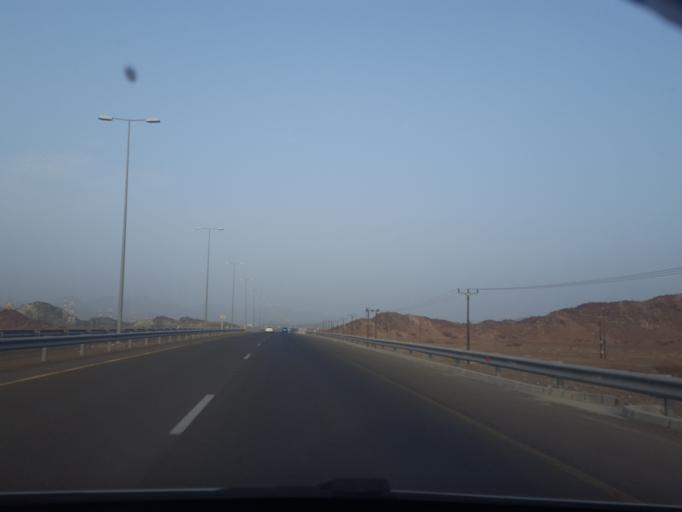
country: OM
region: Al Buraimi
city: Al Buraymi
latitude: 24.2467
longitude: 56.0111
